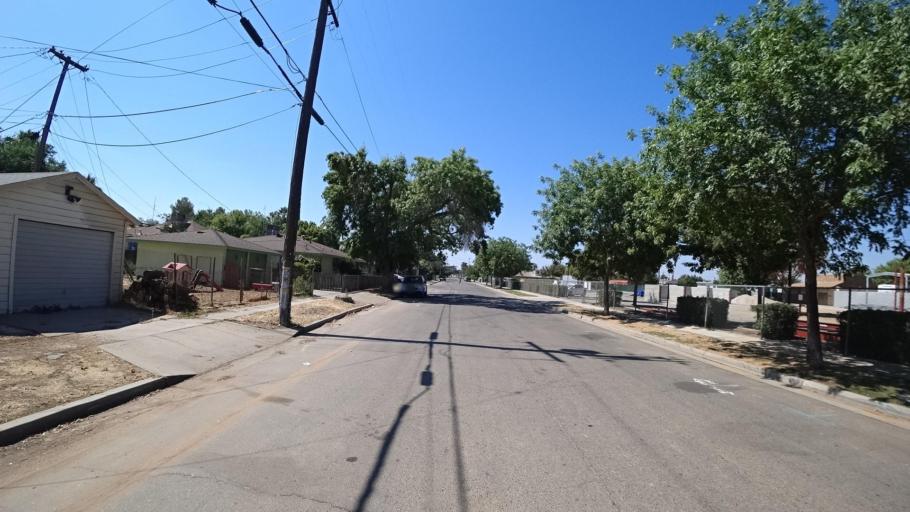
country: US
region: California
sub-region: Fresno County
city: Fresno
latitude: 36.7610
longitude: -119.7770
